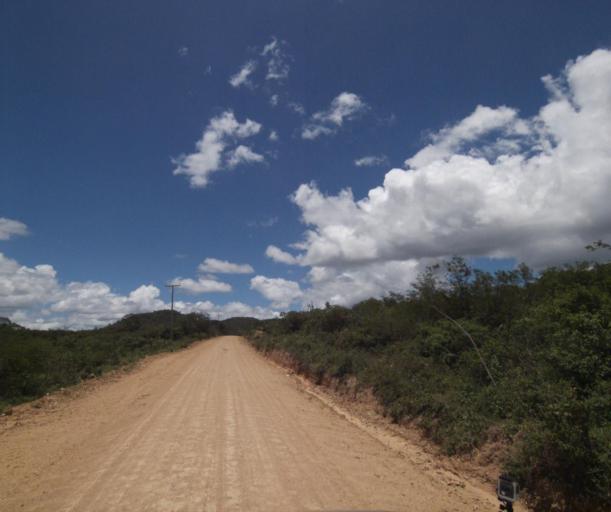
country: BR
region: Bahia
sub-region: Pocoes
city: Pocoes
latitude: -14.3789
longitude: -40.4063
